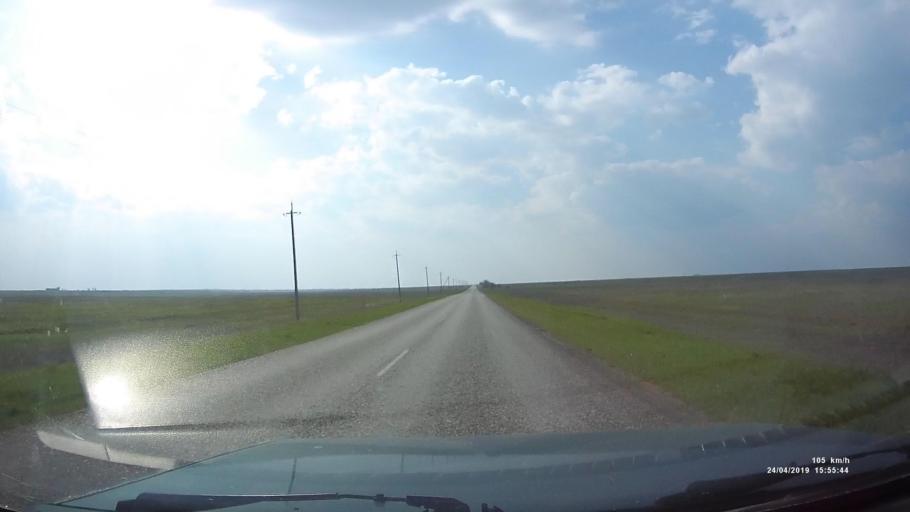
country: RU
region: Kalmykiya
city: Yashalta
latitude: 46.5925
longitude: 42.5433
